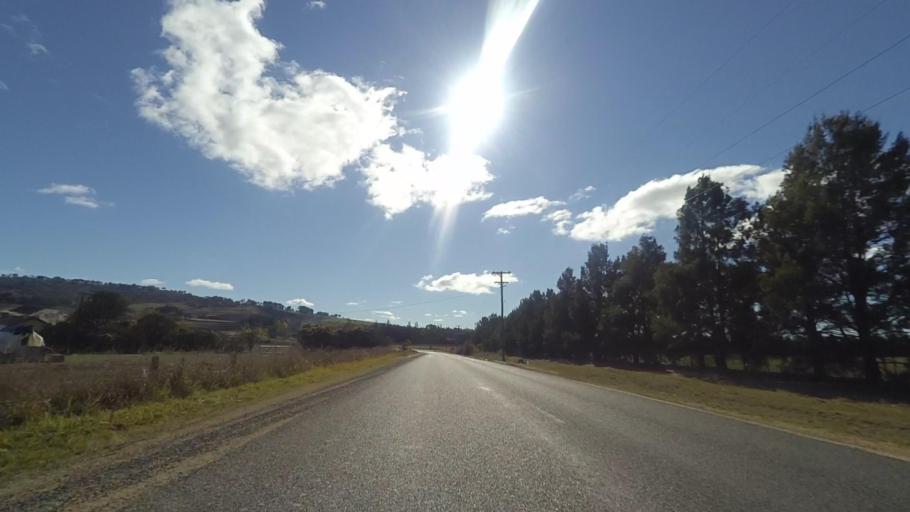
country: AU
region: New South Wales
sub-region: Bathurst Regional
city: Perthville
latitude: -33.4688
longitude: 149.5741
